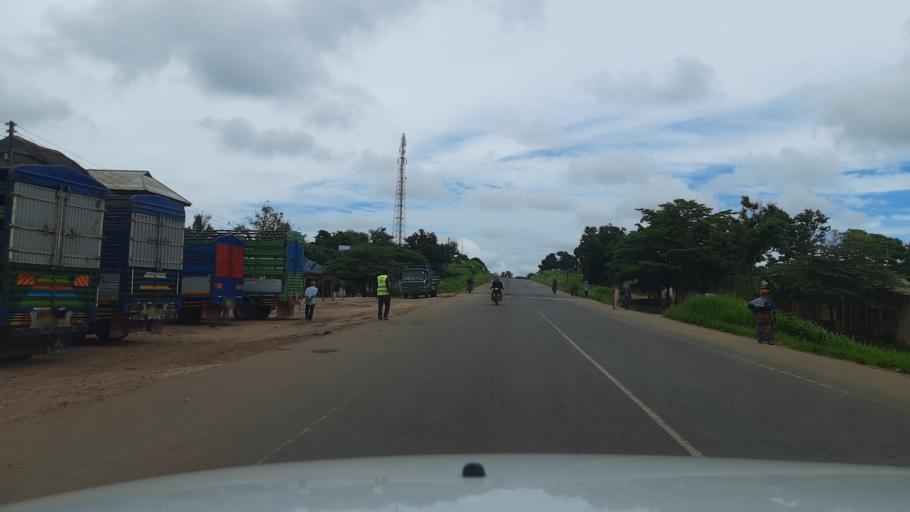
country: TZ
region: Pwani
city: Lugoba
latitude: -6.0781
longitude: 38.2433
